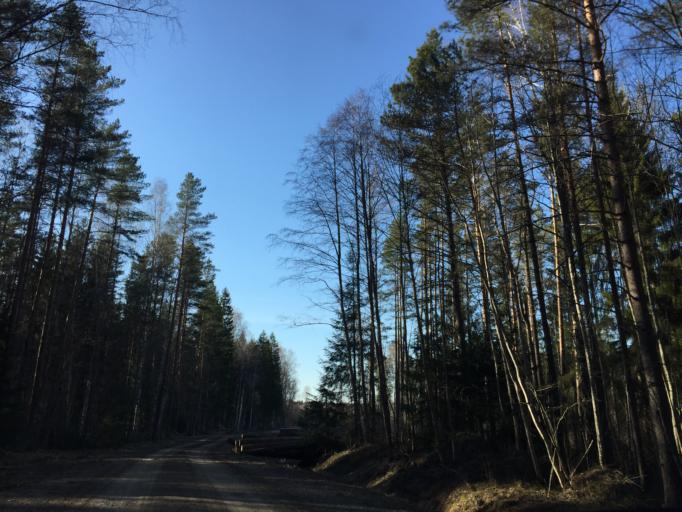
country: EE
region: Ida-Virumaa
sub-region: Sillamaee linn
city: Sillamae
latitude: 59.1462
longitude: 27.8081
